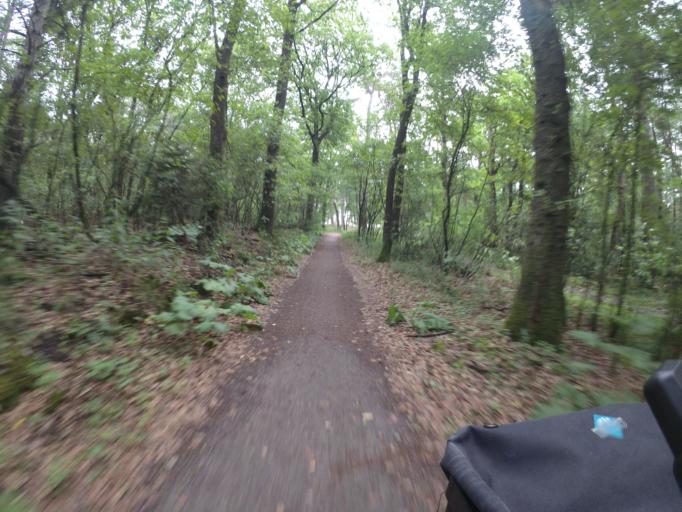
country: NL
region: Drenthe
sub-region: Gemeente Westerveld
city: Dwingeloo
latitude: 52.8077
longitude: 6.3696
